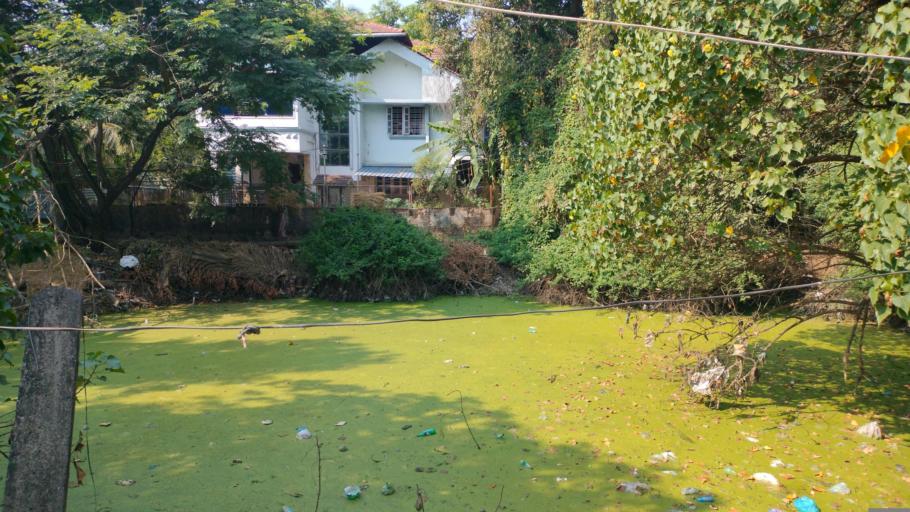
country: IN
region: Maharashtra
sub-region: Thane
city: Virar
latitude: 19.4014
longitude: 72.7910
